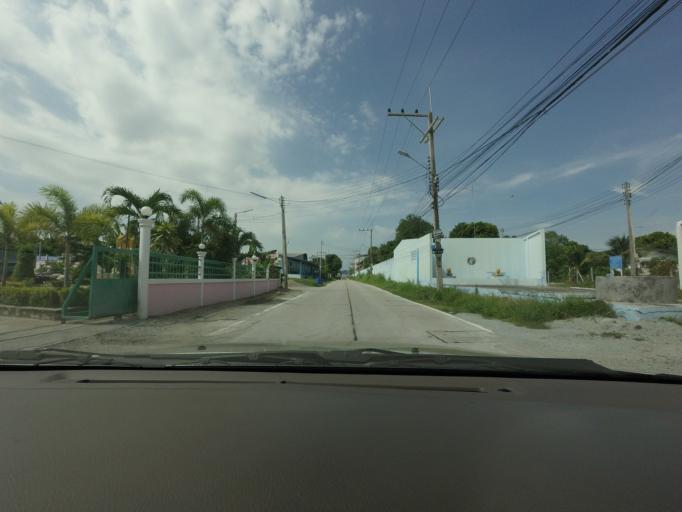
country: TH
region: Chon Buri
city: Chon Buri
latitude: 13.3249
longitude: 101.0027
